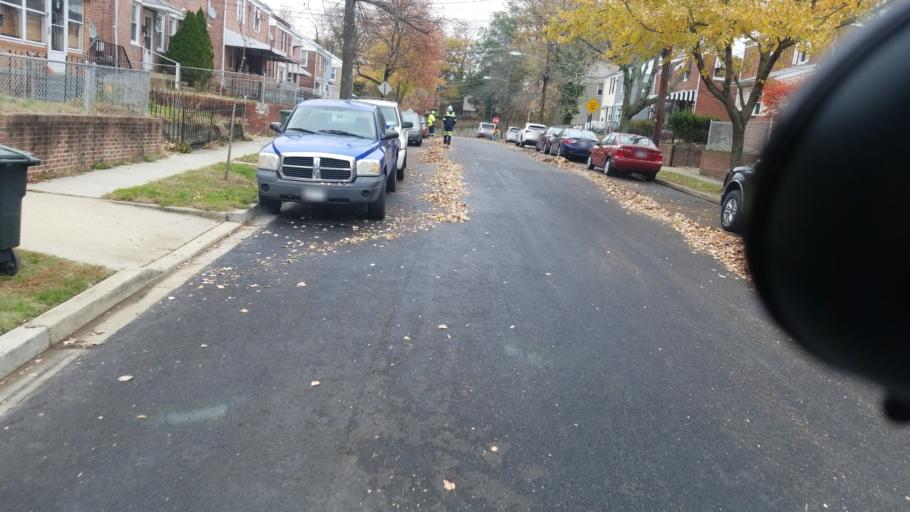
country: US
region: Maryland
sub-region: Prince George's County
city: Capitol Heights
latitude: 38.8848
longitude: -76.9215
